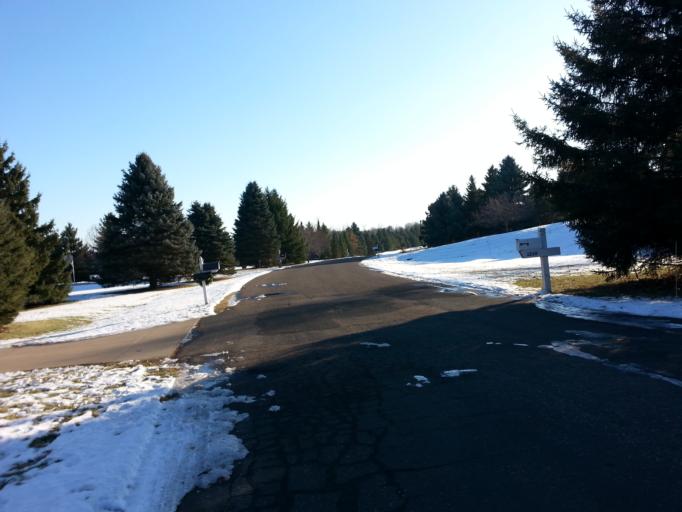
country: US
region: Minnesota
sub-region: Washington County
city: Lake Elmo
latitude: 44.9669
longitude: -92.8301
